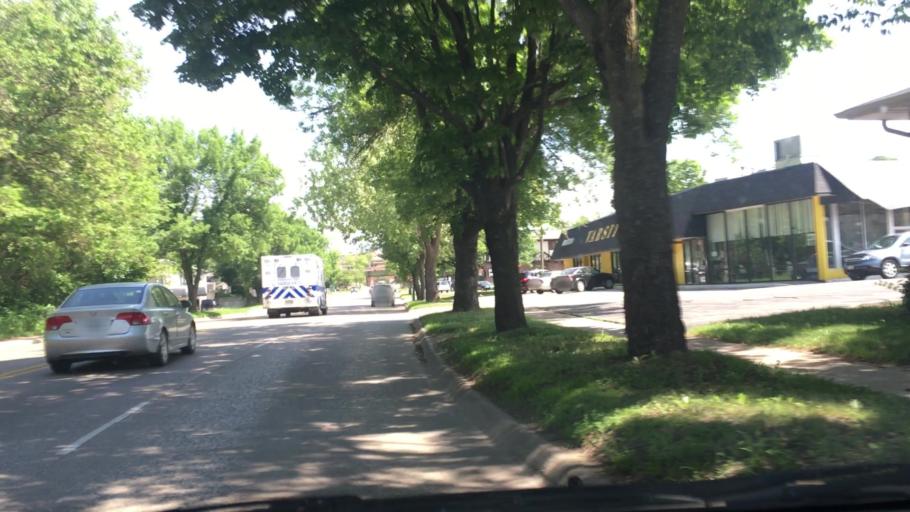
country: US
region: Iowa
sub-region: Johnson County
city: Iowa City
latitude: 41.6503
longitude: -91.5319
